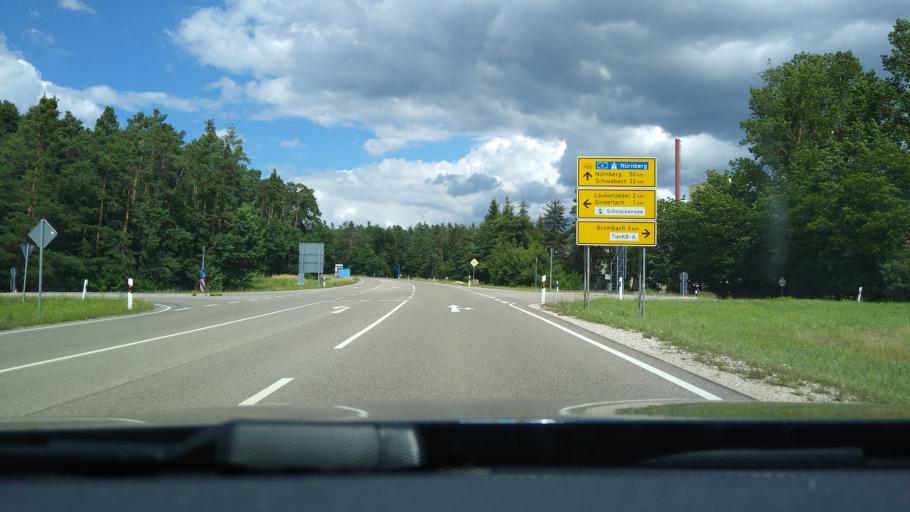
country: DE
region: Bavaria
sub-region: Regierungsbezirk Mittelfranken
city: Gunzenhausen
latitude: 49.1315
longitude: 10.7755
